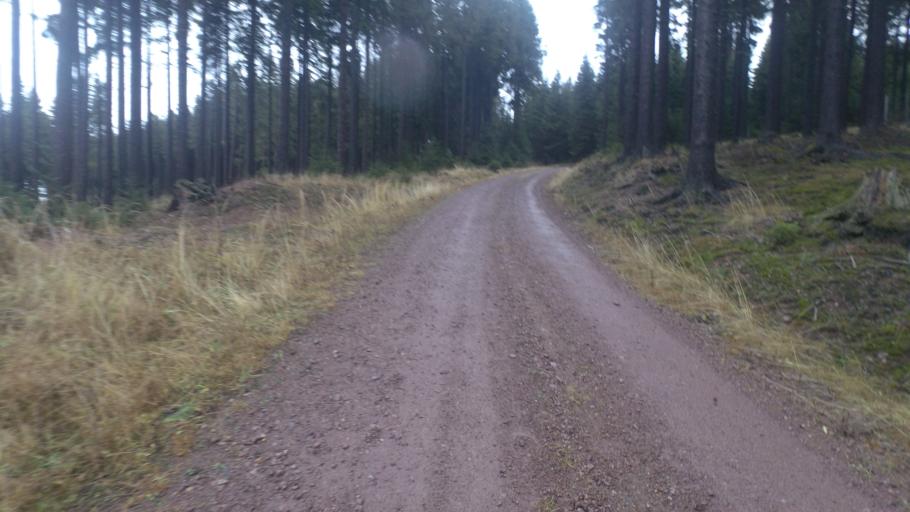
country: DE
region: Thuringia
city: Oberhof
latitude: 50.7167
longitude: 10.7572
